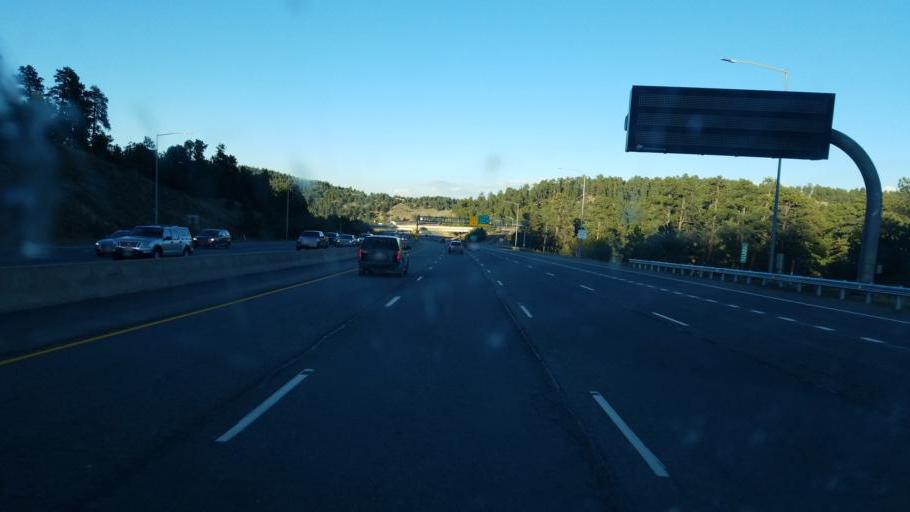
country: US
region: Colorado
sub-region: Jefferson County
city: Genesee
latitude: 39.7085
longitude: -105.3201
